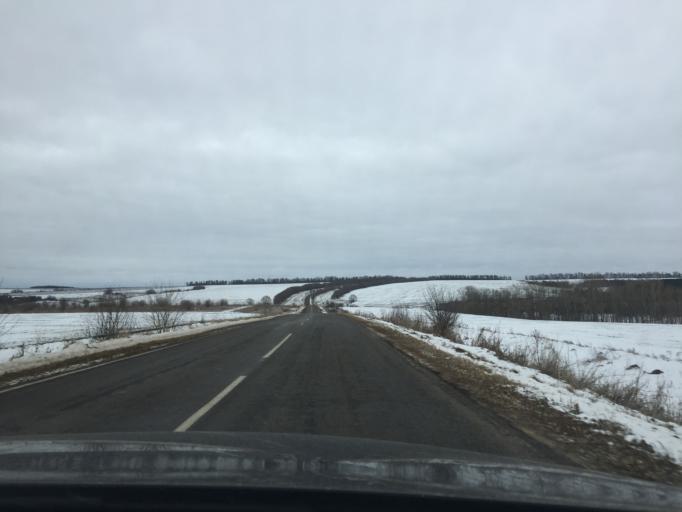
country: RU
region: Tula
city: Teploye
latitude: 53.8061
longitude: 37.5522
